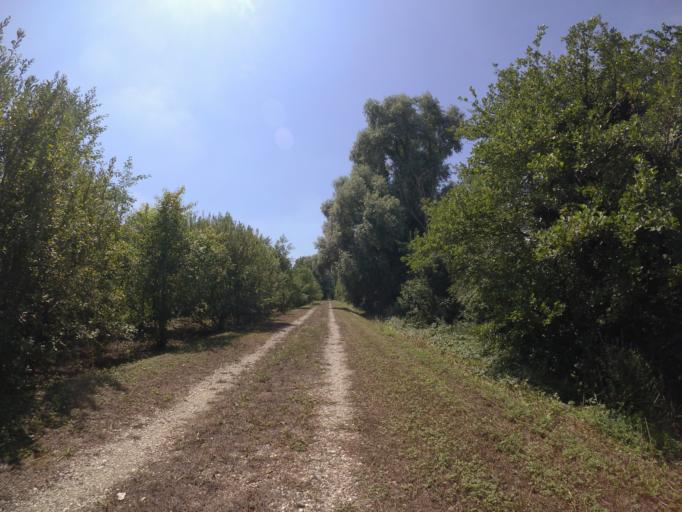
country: IT
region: Friuli Venezia Giulia
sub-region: Provincia di Udine
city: Rivignano
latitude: 45.8981
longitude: 13.0675
